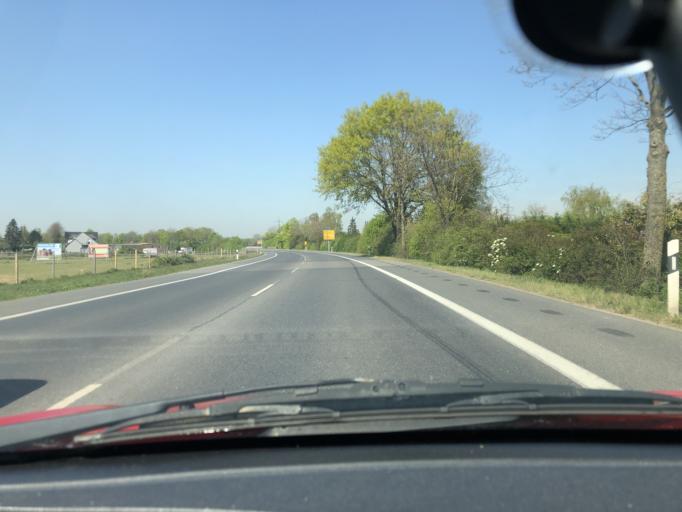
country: DE
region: North Rhine-Westphalia
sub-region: Regierungsbezirk Dusseldorf
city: Kamp-Lintfort
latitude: 51.5031
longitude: 6.5688
